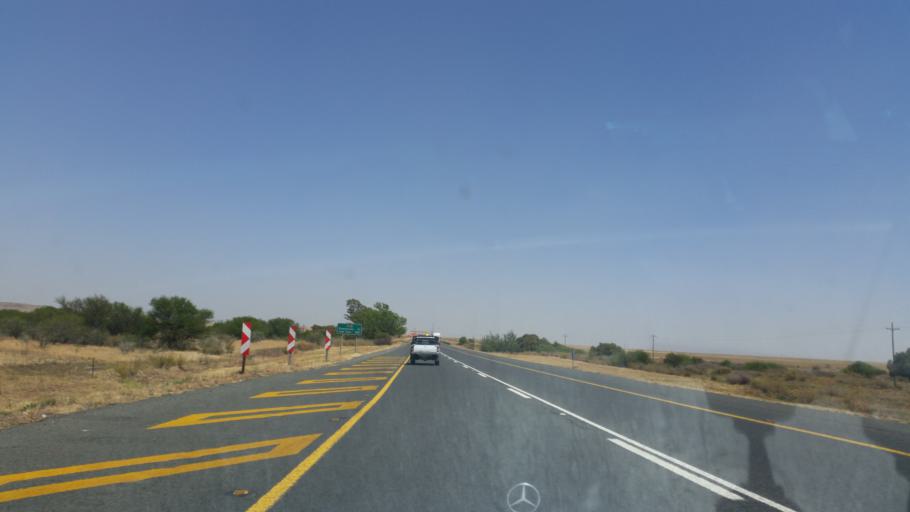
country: ZA
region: Orange Free State
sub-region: Lejweleputswa District Municipality
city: Brandfort
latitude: -28.7902
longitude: 26.7017
